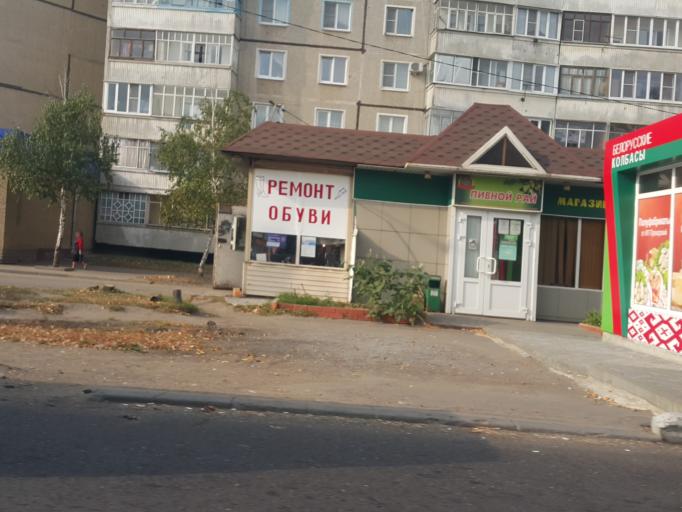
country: RU
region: Tambov
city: Bokino
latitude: 52.6764
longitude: 41.4655
